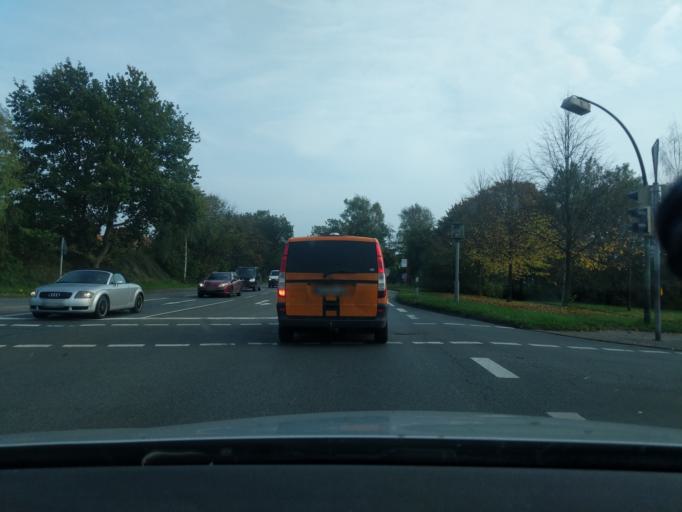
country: DE
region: Lower Saxony
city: Stade
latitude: 53.5865
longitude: 9.4582
